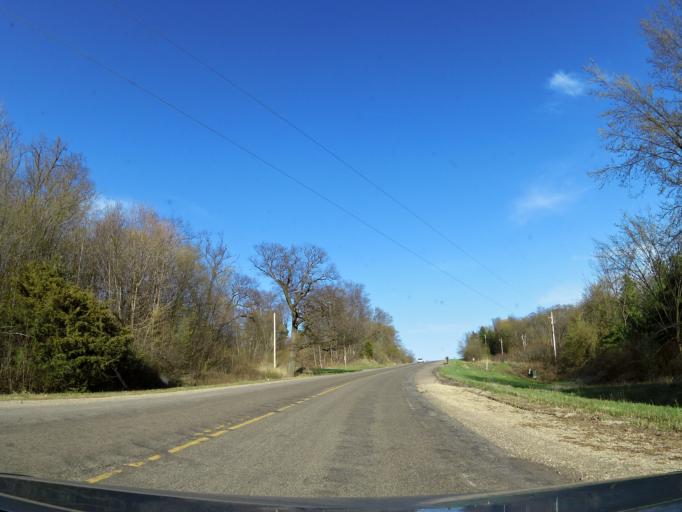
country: US
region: Wisconsin
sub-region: Pierce County
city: River Falls
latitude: 44.8625
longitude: -92.6964
